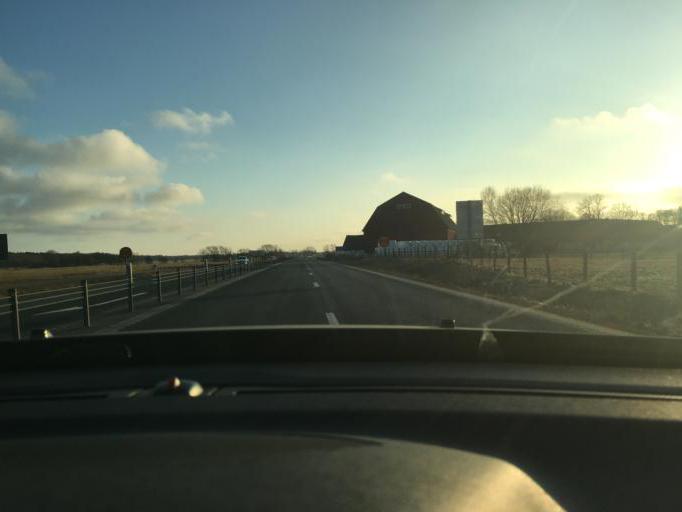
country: SE
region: Halland
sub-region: Varbergs Kommun
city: Varberg
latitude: 57.1439
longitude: 12.2672
